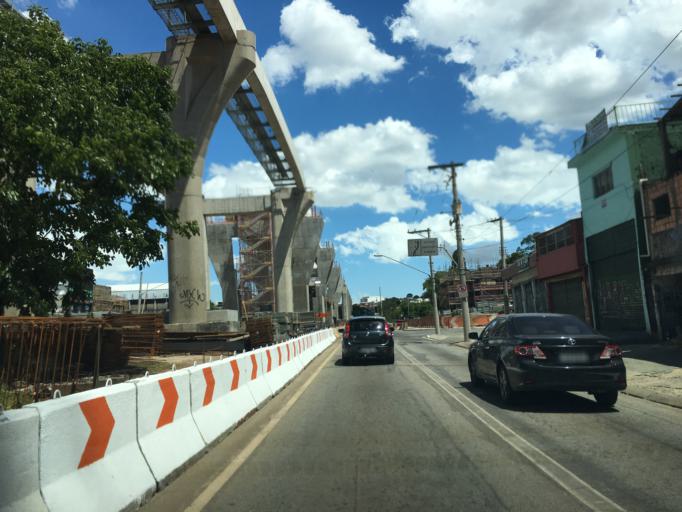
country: BR
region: Sao Paulo
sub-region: Sao Caetano Do Sul
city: Sao Caetano do Sul
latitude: -23.5949
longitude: -46.5384
